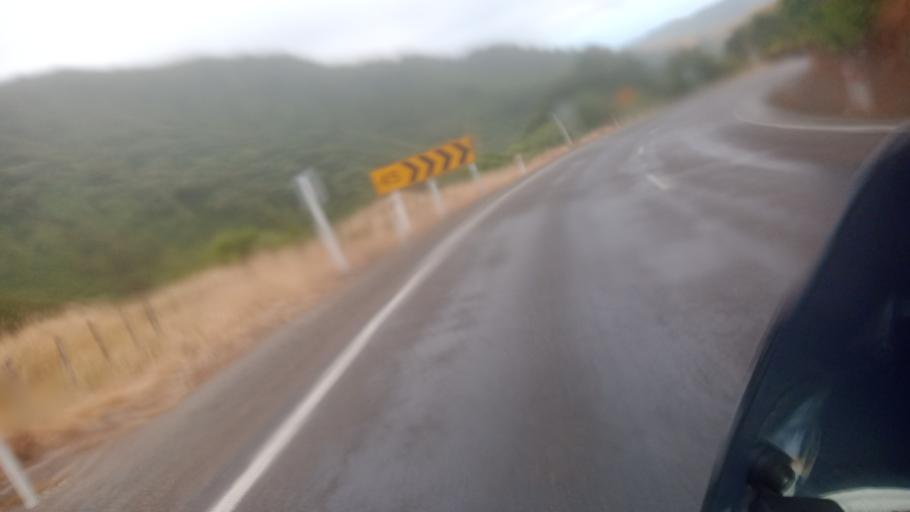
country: NZ
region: Bay of Plenty
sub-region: Opotiki District
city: Opotiki
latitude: -38.3573
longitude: 177.4529
